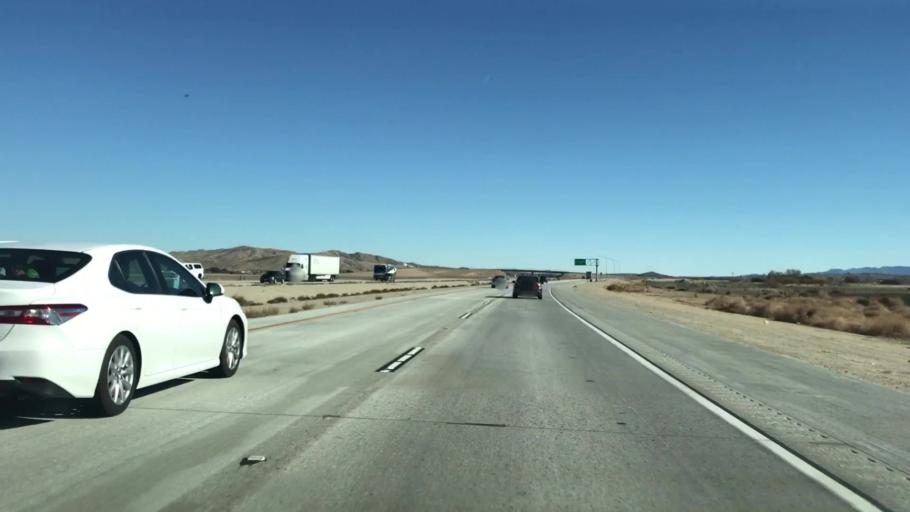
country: US
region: California
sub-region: San Bernardino County
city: Lenwood
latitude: 34.9154
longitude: -117.1303
